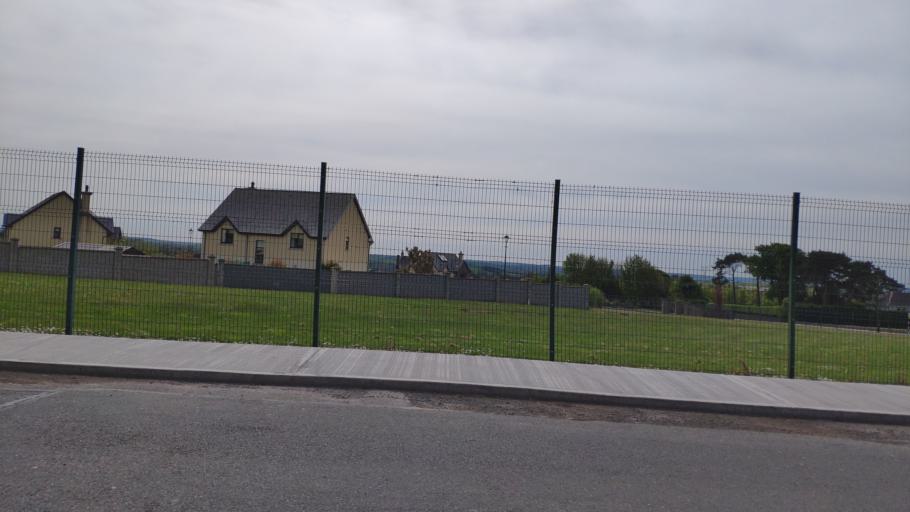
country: IE
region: Munster
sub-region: County Cork
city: Blarney
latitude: 51.9826
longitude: -8.5140
